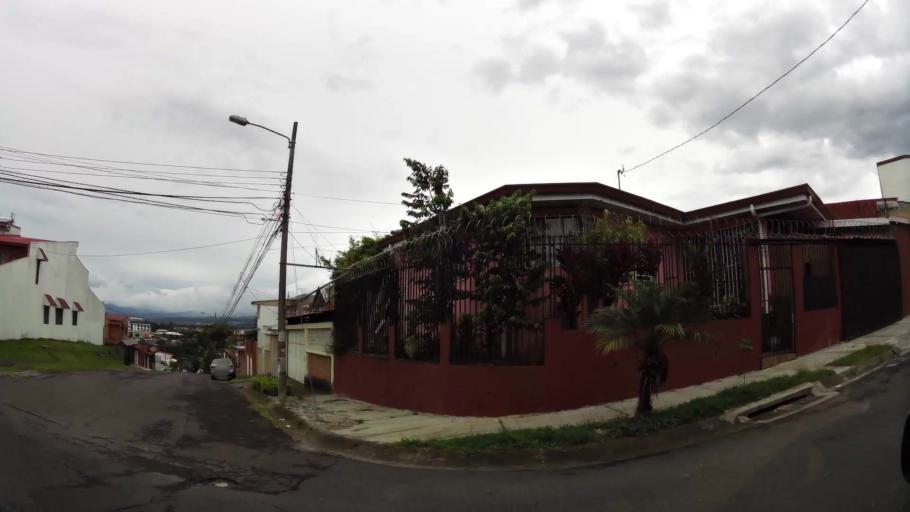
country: CR
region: San Jose
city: Calle Blancos
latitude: 9.9522
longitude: -84.0648
